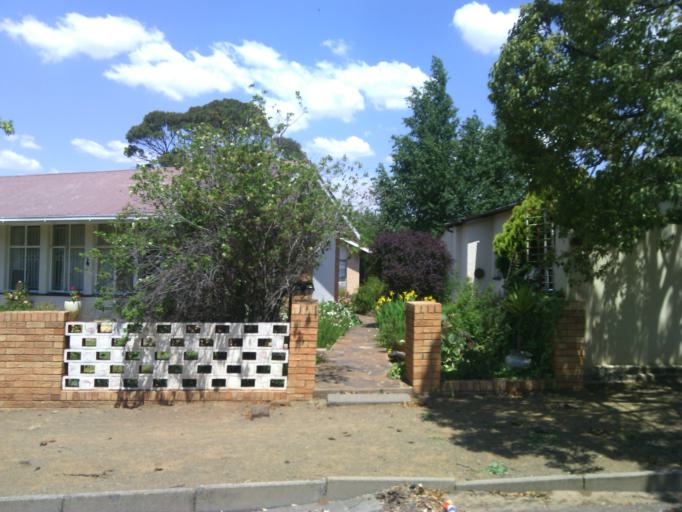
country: ZA
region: Orange Free State
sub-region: Xhariep District Municipality
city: Dewetsdorp
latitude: -29.5837
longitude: 26.6614
